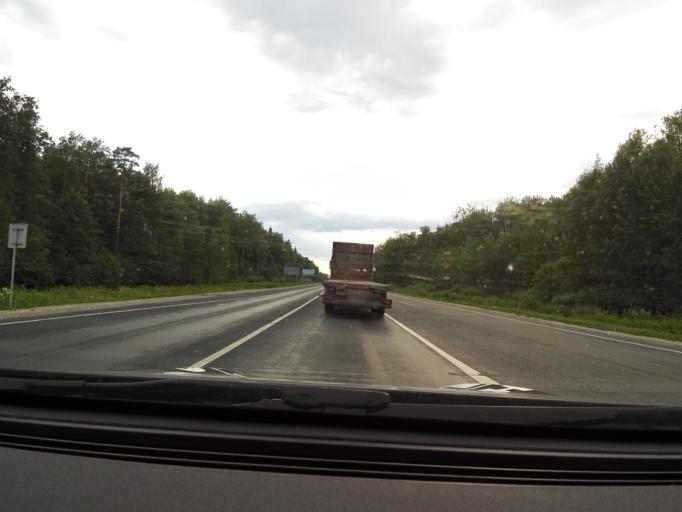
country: RU
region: Vladimir
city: Raduzhnyy
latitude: 56.0652
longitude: 40.3593
